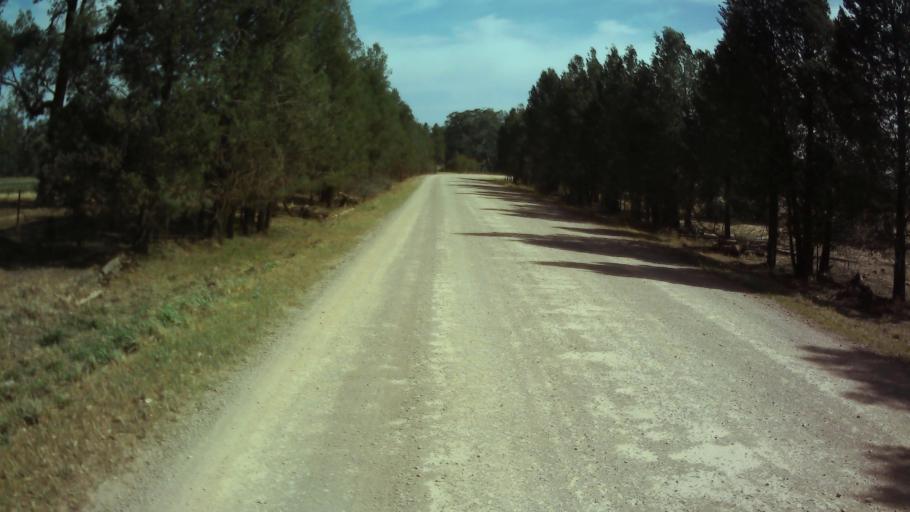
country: AU
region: New South Wales
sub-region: Weddin
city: Grenfell
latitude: -34.0386
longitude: 148.0806
